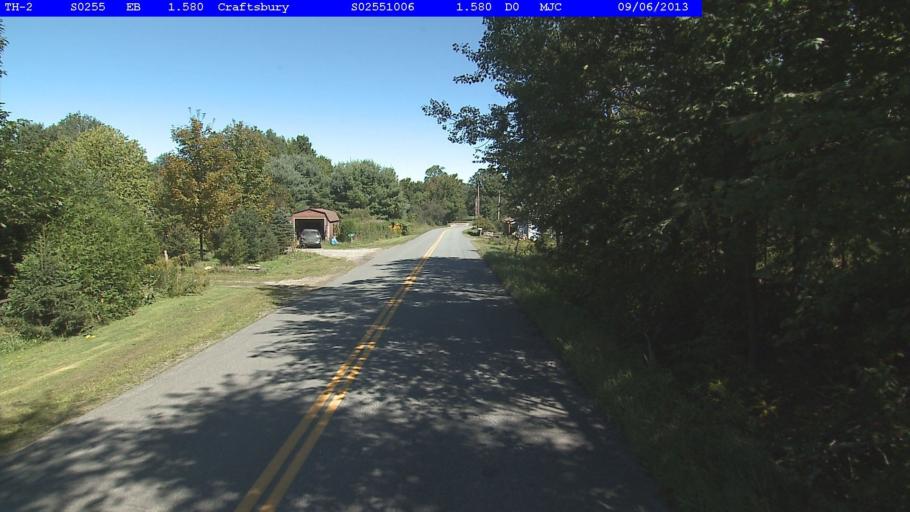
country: US
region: Vermont
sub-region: Caledonia County
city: Hardwick
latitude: 44.6398
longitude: -72.3444
